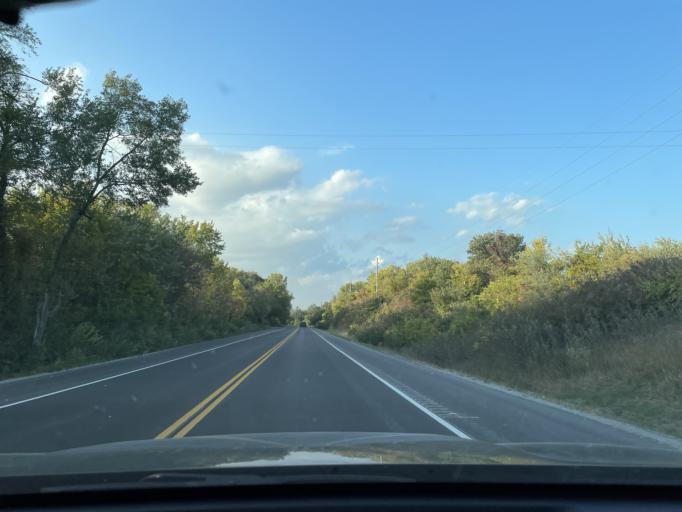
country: US
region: Missouri
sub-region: Andrew County
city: Country Club Village
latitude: 39.8484
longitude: -94.8696
